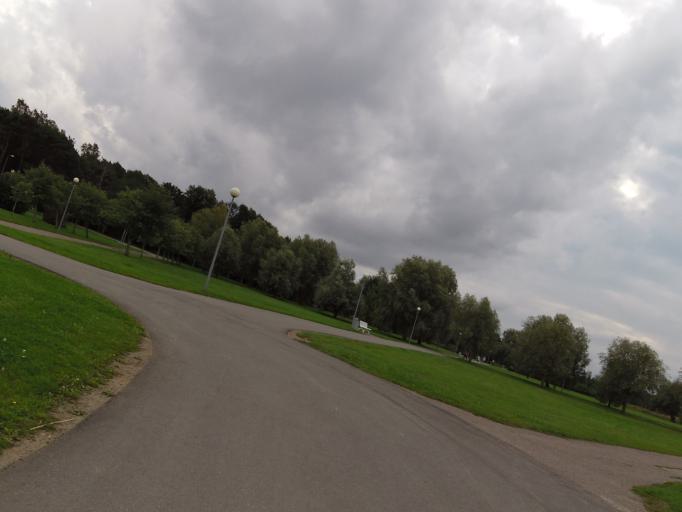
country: EE
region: Harju
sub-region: Tallinna linn
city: Tallinn
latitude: 59.4380
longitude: 24.6828
